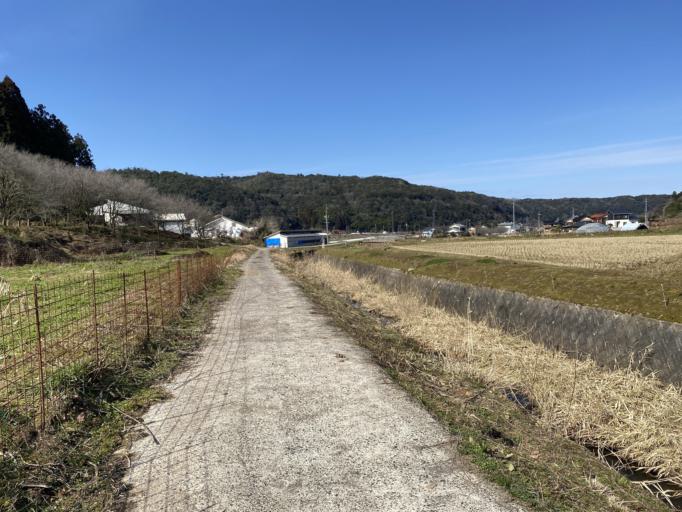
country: JP
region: Tottori
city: Kurayoshi
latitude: 35.4938
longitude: 133.9868
